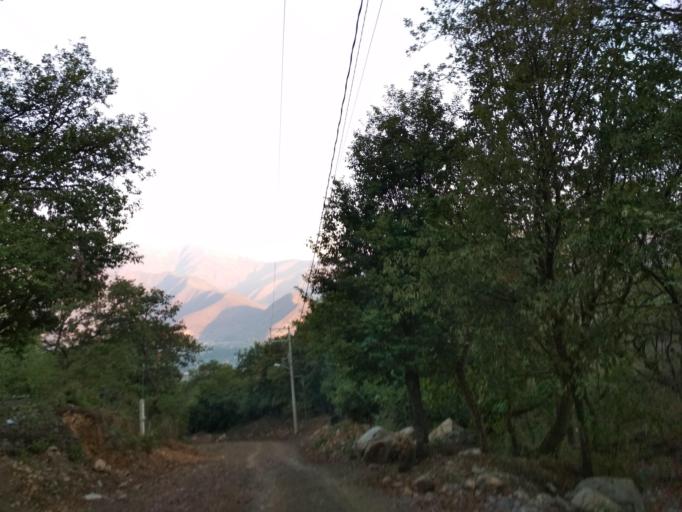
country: MX
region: Veracruz
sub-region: Nogales
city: Taza de Agua Ojo Zarco
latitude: 18.7752
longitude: -97.1897
